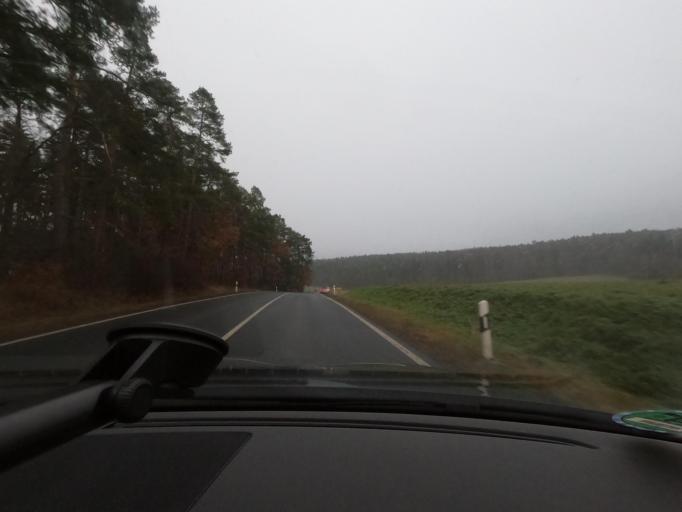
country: DE
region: Thuringia
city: Behringen
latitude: 50.7820
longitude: 10.9968
